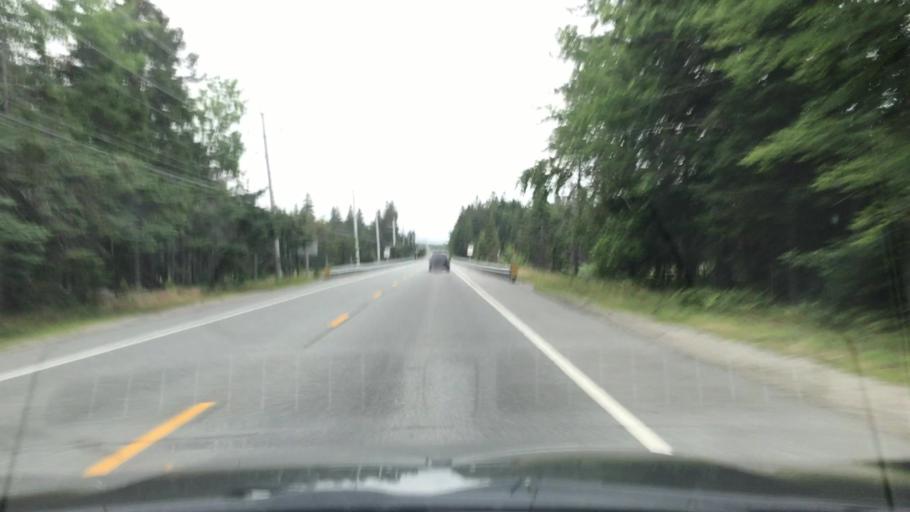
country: US
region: Maine
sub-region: Hancock County
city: Trenton
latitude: 44.4240
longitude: -68.3648
